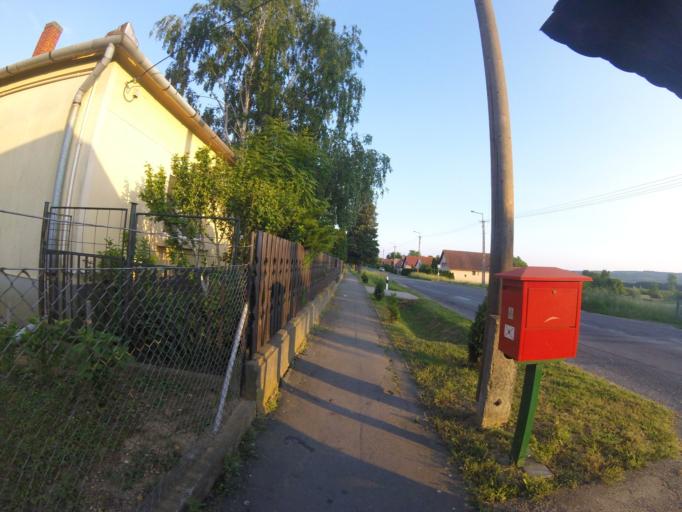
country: HU
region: Zala
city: Zalaszentgrot
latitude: 46.8681
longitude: 17.1156
